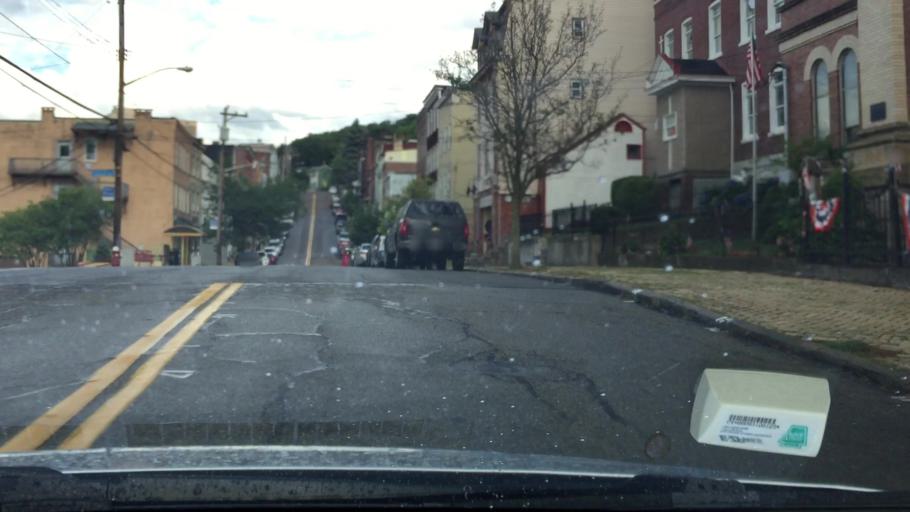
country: US
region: Pennsylvania
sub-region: Allegheny County
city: Bloomfield
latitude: 40.4566
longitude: -79.9680
